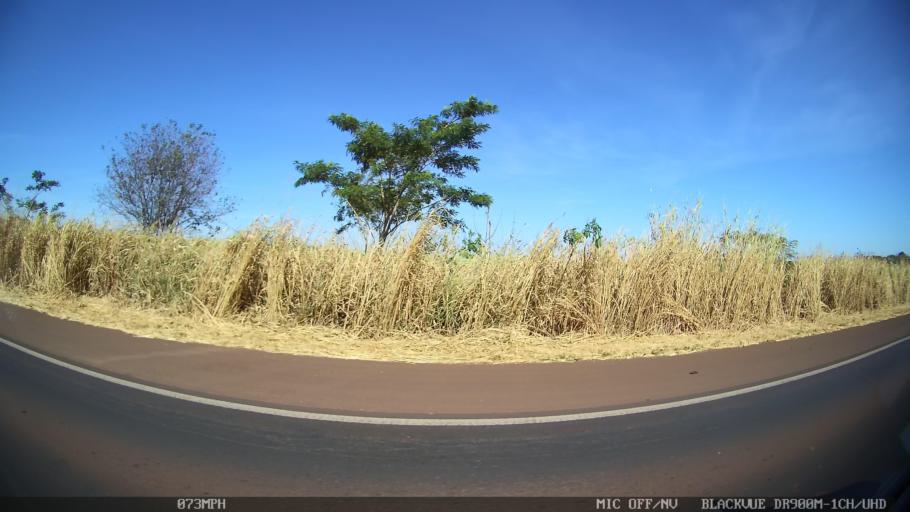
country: BR
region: Sao Paulo
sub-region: Barretos
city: Barretos
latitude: -20.4963
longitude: -48.5326
